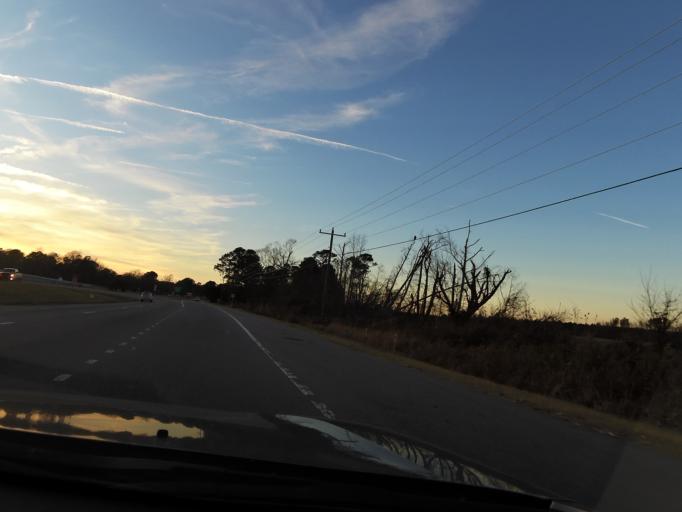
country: US
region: Virginia
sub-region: Southampton County
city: Courtland
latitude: 36.6955
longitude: -77.0361
